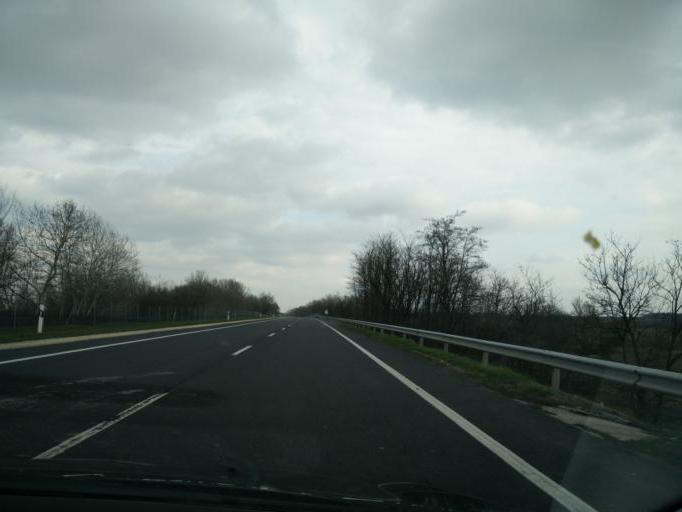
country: HU
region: Gyor-Moson-Sopron
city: Toltestava
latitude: 47.6953
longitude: 17.7822
